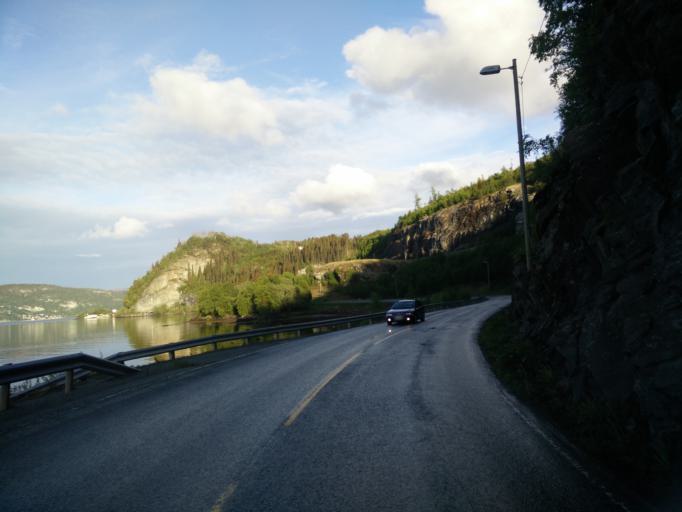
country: NO
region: Sor-Trondelag
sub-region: Skaun
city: Borsa
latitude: 63.3261
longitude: 10.1129
